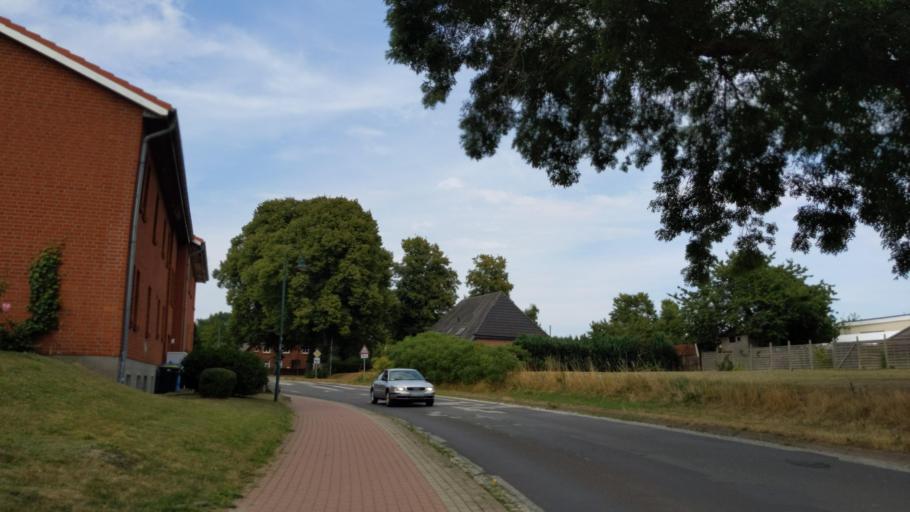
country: DE
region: Schleswig-Holstein
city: Gross Gronau
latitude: 53.8310
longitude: 10.8108
